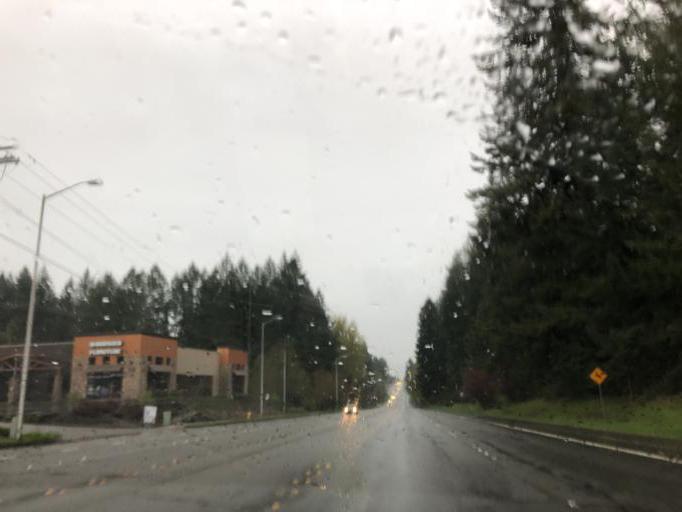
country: US
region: Washington
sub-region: Thurston County
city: Tanglewilde-Thompson Place
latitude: 47.0502
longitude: -122.7995
